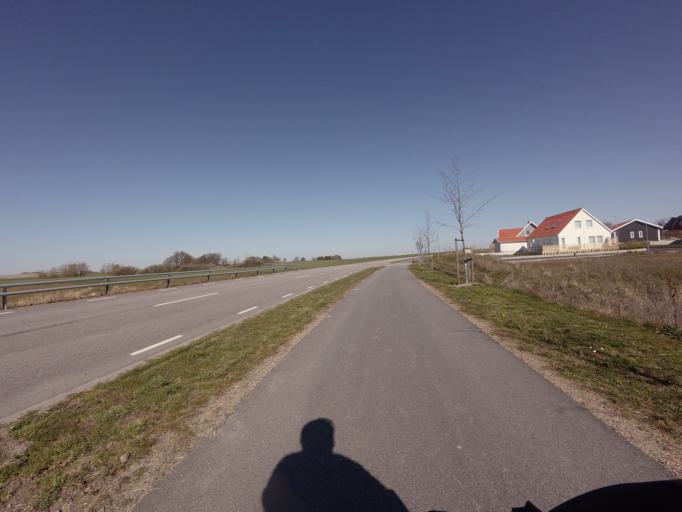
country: SE
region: Skane
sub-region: Malmo
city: Oxie
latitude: 55.4670
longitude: 13.1308
